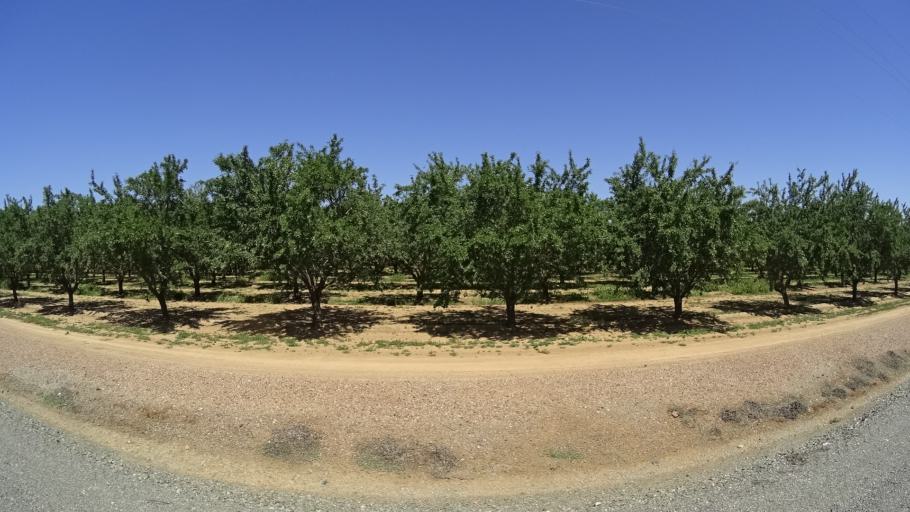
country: US
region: California
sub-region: Glenn County
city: Hamilton City
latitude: 39.7666
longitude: -122.0894
